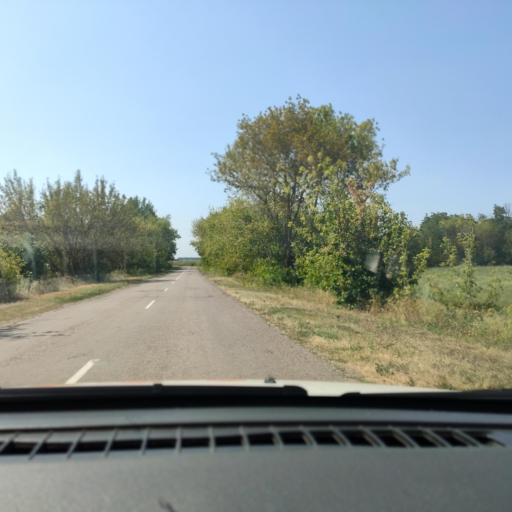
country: RU
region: Voronezj
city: Imeni Pervogo Maya
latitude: 50.7134
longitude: 39.3414
